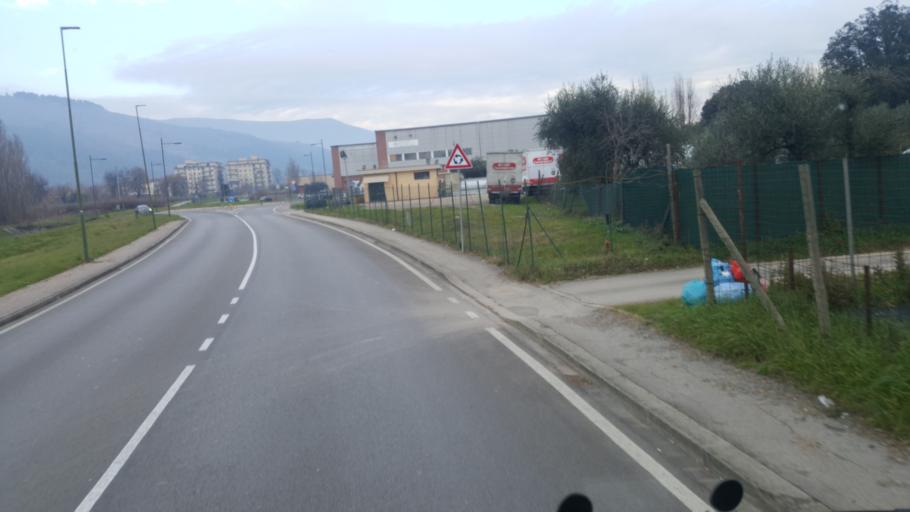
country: IT
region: Tuscany
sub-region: Province of Florence
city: Calenzano
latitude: 43.8533
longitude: 11.1419
